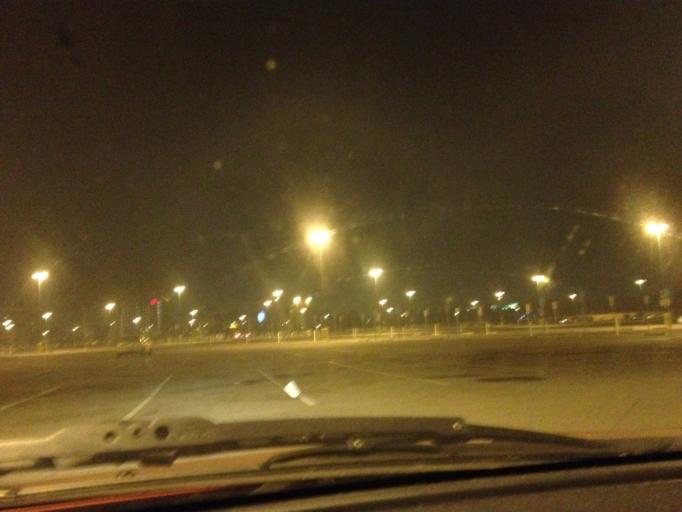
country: US
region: California
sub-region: Orange County
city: Anaheim
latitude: 33.7995
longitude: -117.9105
